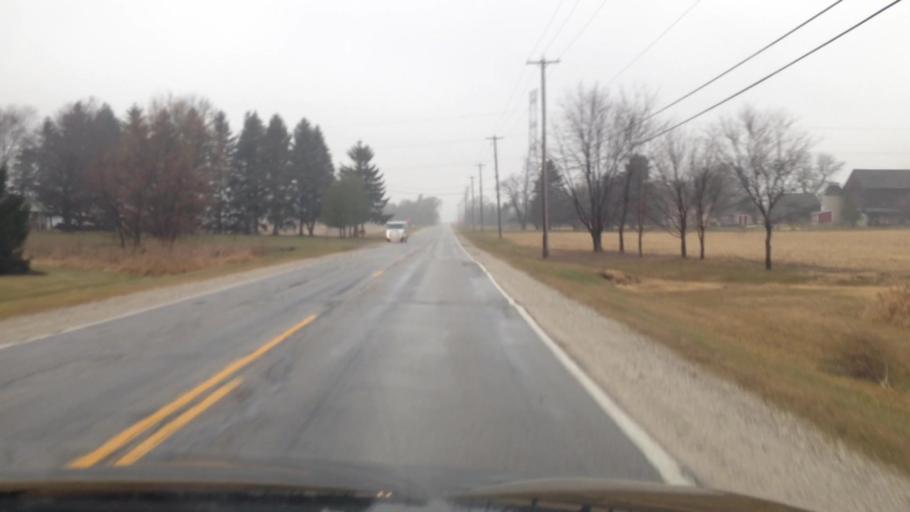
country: US
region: Wisconsin
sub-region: Washington County
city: Germantown
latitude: 43.2502
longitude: -88.1486
